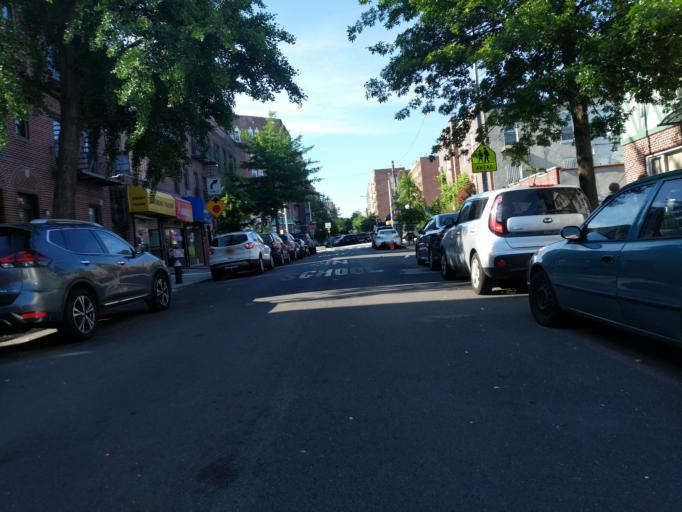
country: US
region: New York
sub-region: Queens County
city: Long Island City
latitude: 40.7392
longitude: -73.9242
